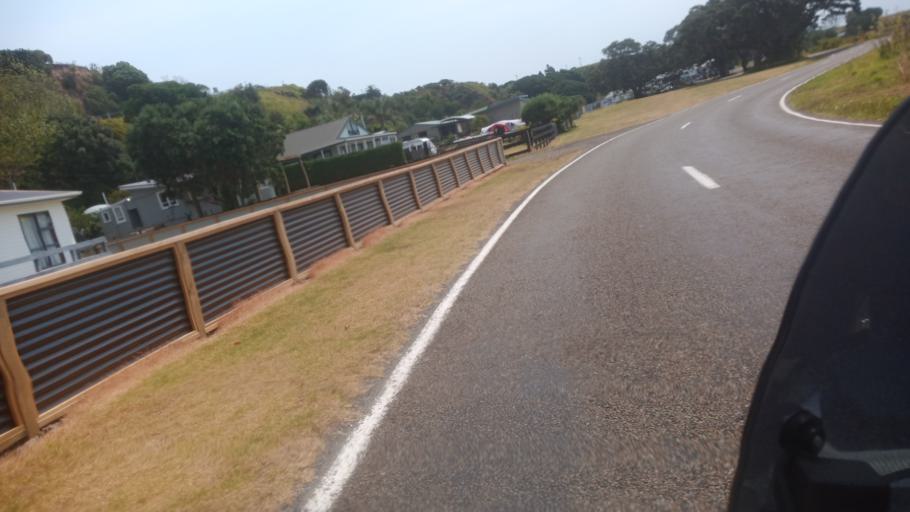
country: NZ
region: Bay of Plenty
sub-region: Opotiki District
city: Opotiki
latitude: -37.6180
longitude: 177.9109
